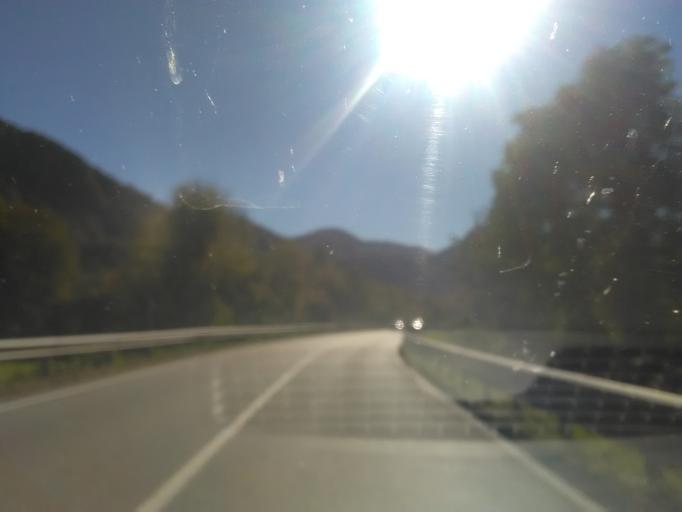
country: IT
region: Piedmont
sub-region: Provincia di Vercelli
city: Varallo
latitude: 45.7952
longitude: 8.2710
